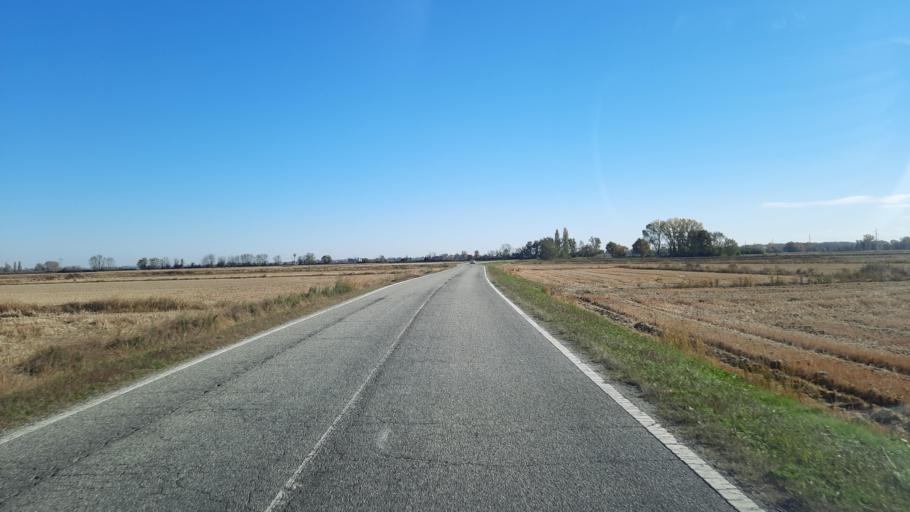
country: IT
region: Piedmont
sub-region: Provincia di Alessandria
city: Villanova Monferrato
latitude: 45.1837
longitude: 8.4410
